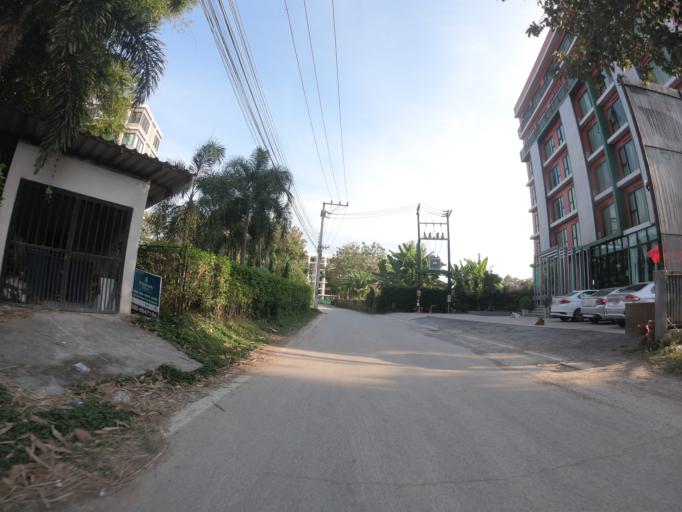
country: TH
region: Chiang Mai
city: Chiang Mai
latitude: 18.8224
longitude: 98.9630
